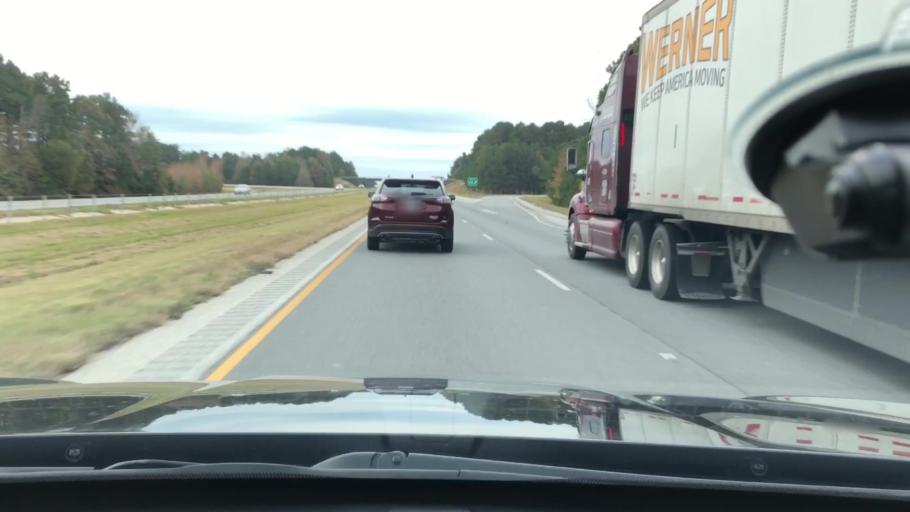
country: US
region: Arkansas
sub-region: Clark County
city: Arkadelphia
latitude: 34.0695
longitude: -93.1226
